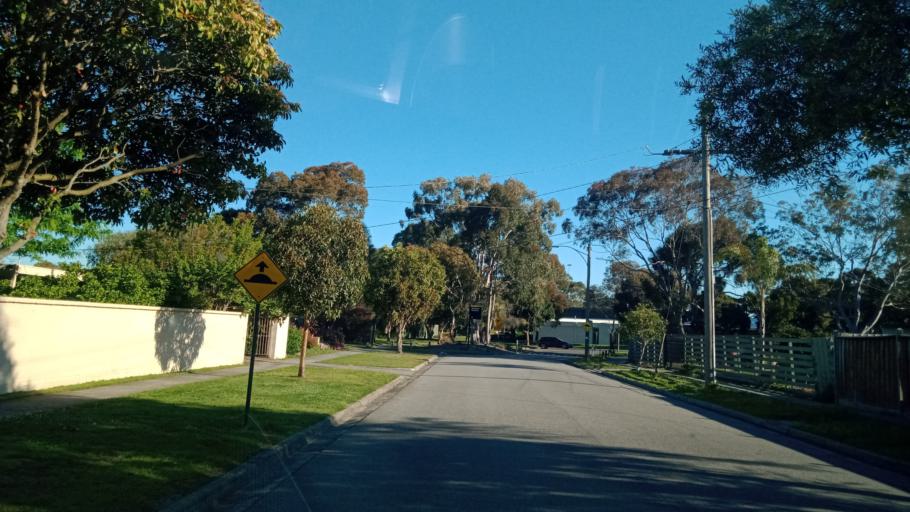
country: AU
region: Victoria
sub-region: Greater Dandenong
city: Noble Park North
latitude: -37.9324
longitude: 145.1781
